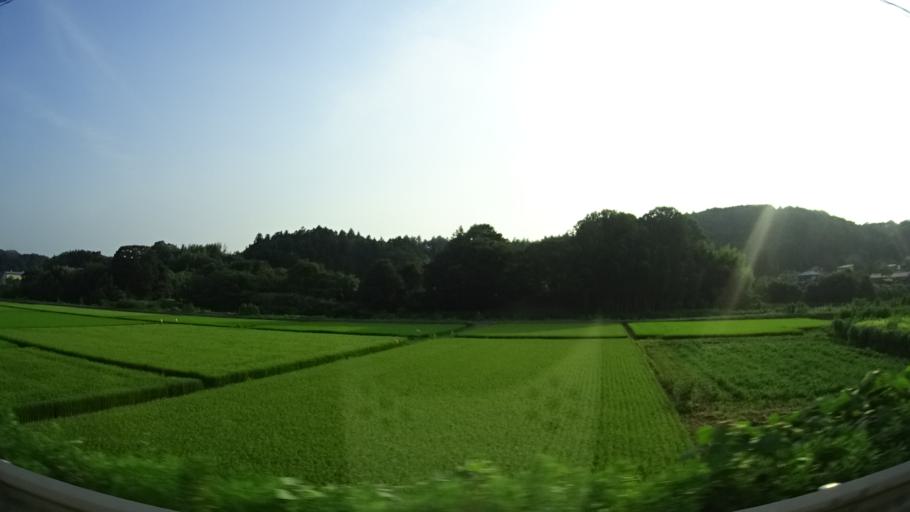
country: JP
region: Tochigi
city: Karasuyama
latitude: 36.6283
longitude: 140.1531
